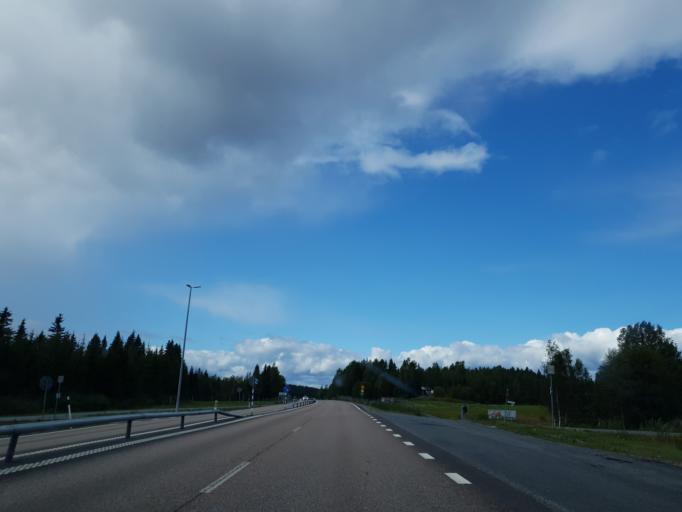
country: SE
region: Vaesternorrland
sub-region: OErnskoeldsviks Kommun
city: Ornskoldsvik
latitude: 63.3017
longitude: 18.8609
